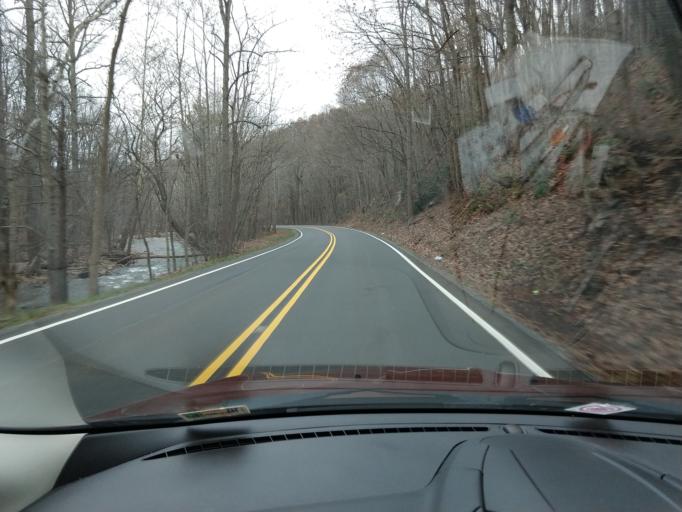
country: US
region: West Virginia
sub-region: Greenbrier County
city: White Sulphur Springs
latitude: 37.7254
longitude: -80.2208
